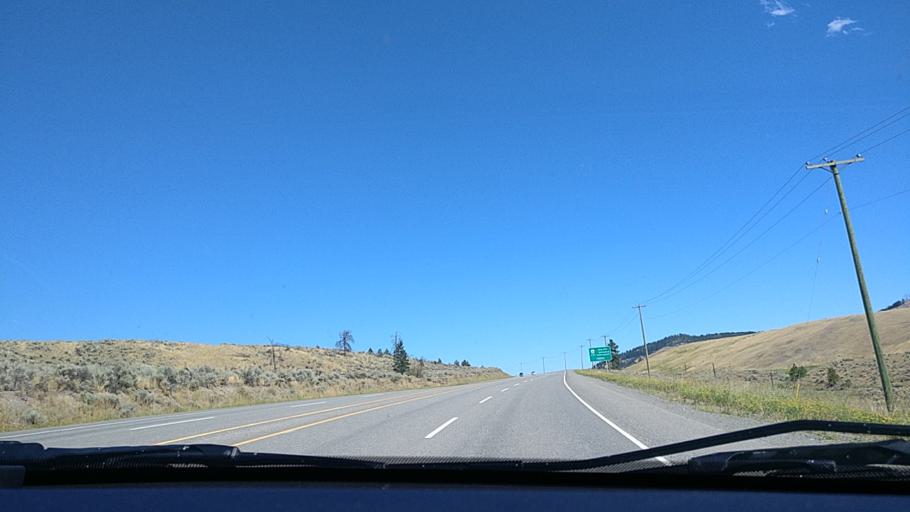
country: CA
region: British Columbia
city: Kamloops
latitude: 50.6693
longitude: -120.4809
